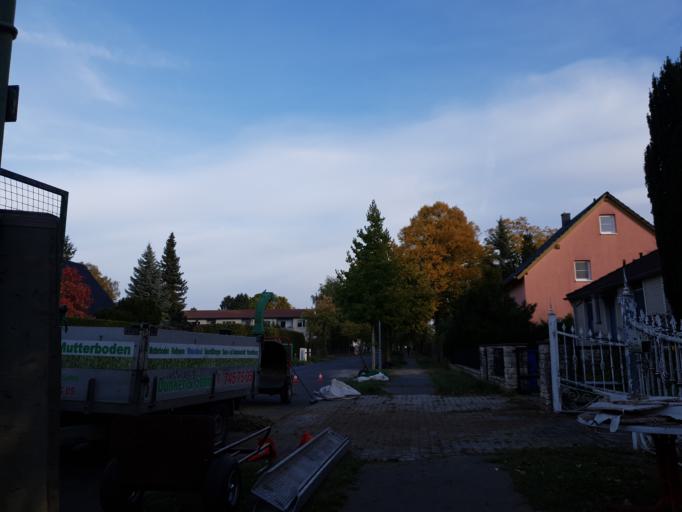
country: DE
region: Berlin
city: Lichtenrade
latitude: 52.3867
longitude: 13.4216
